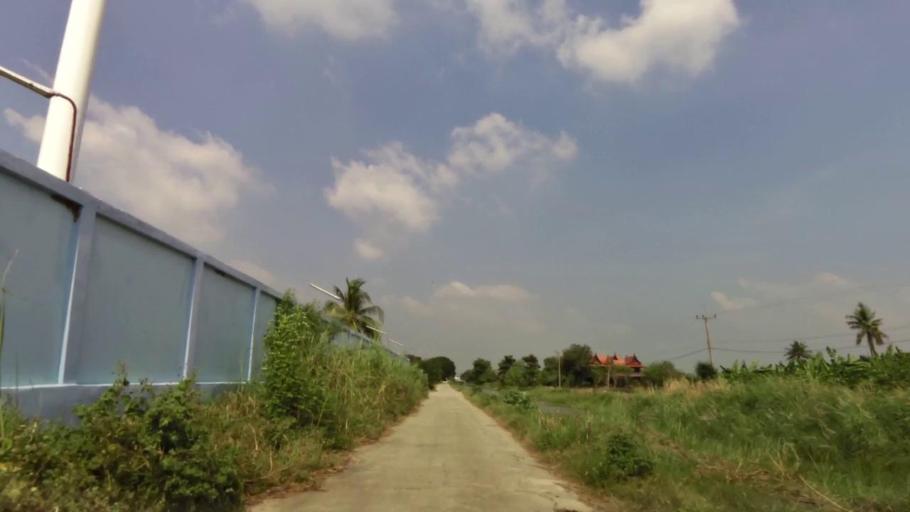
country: TH
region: Ang Thong
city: Ang Thong
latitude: 14.6049
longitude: 100.3997
